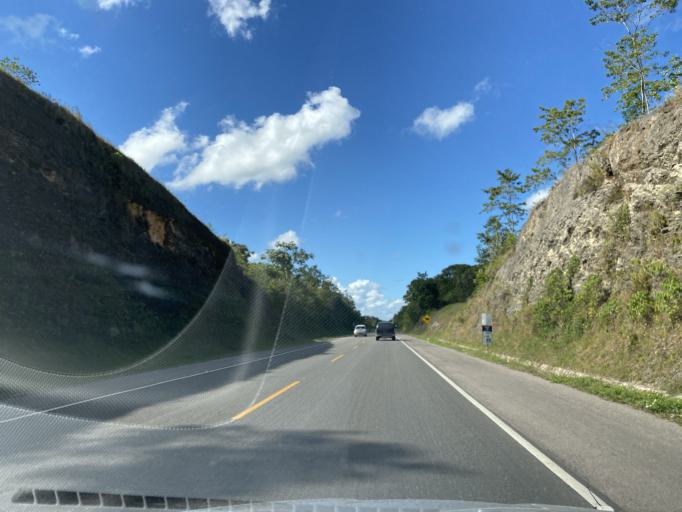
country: DO
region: Monte Plata
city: Sabana Grande de Boya
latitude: 18.9700
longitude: -69.7789
